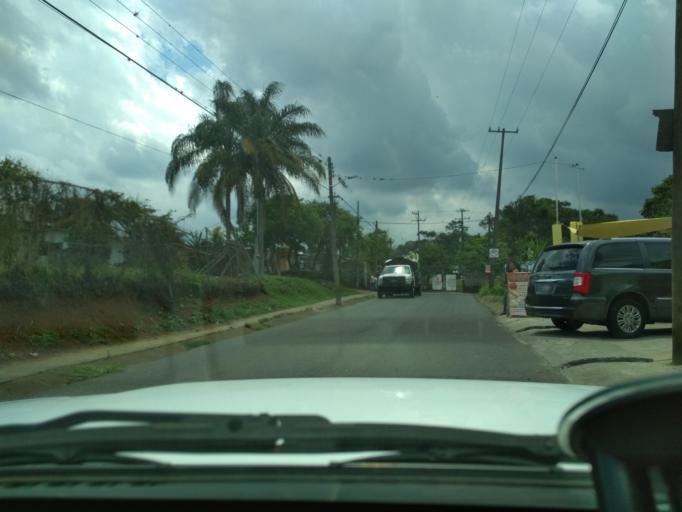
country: MX
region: Veracruz
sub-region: Cordoba
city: San Jose de Abajo [Unidad Habitacional]
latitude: 18.9225
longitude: -96.9647
